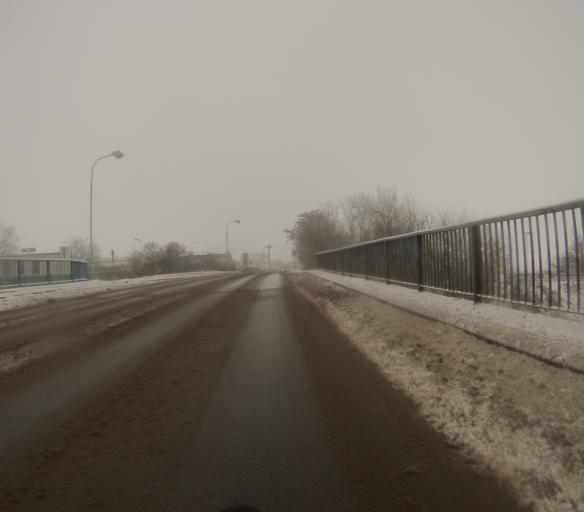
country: CZ
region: South Moravian
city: Strelice
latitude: 49.1564
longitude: 16.5047
